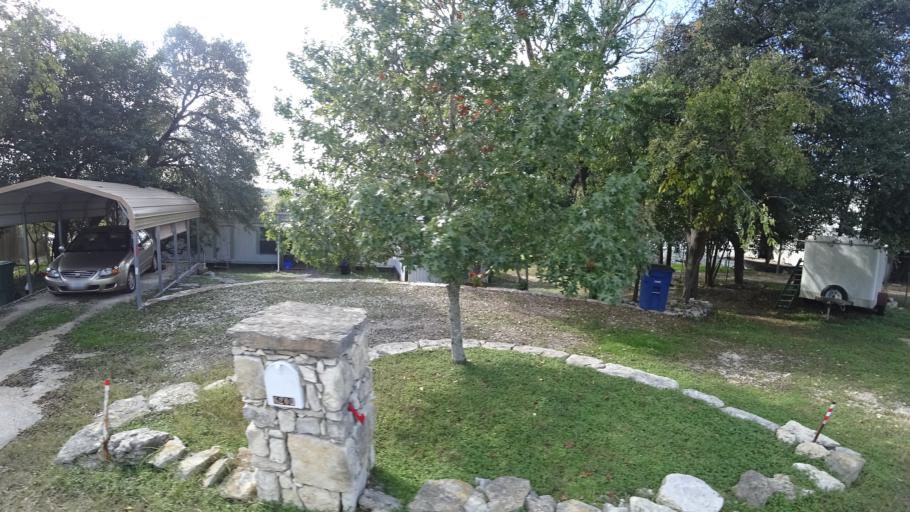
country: US
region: Texas
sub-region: Travis County
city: Barton Creek
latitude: 30.2451
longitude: -97.8795
